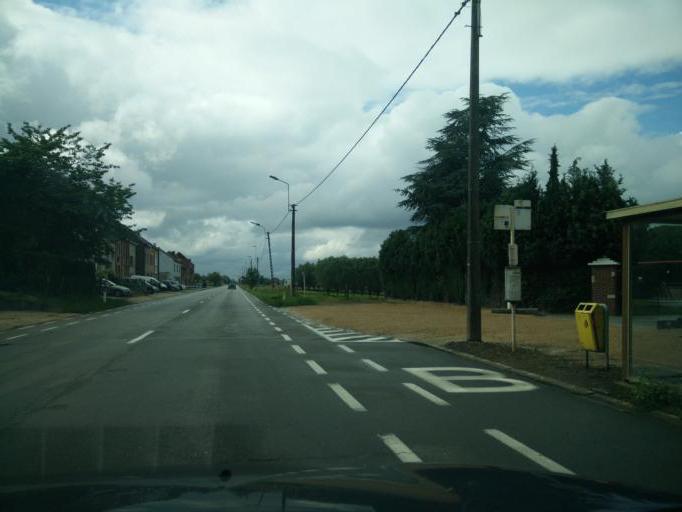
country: BE
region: Flanders
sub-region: Provincie Oost-Vlaanderen
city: Ninove
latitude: 50.8076
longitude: 4.0556
